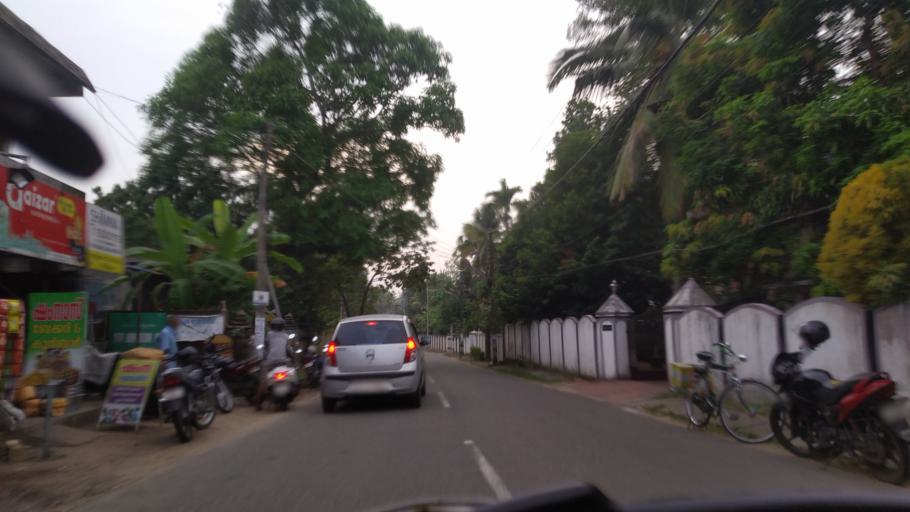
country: IN
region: Kerala
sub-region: Ernakulam
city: Elur
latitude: 10.1349
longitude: 76.2478
